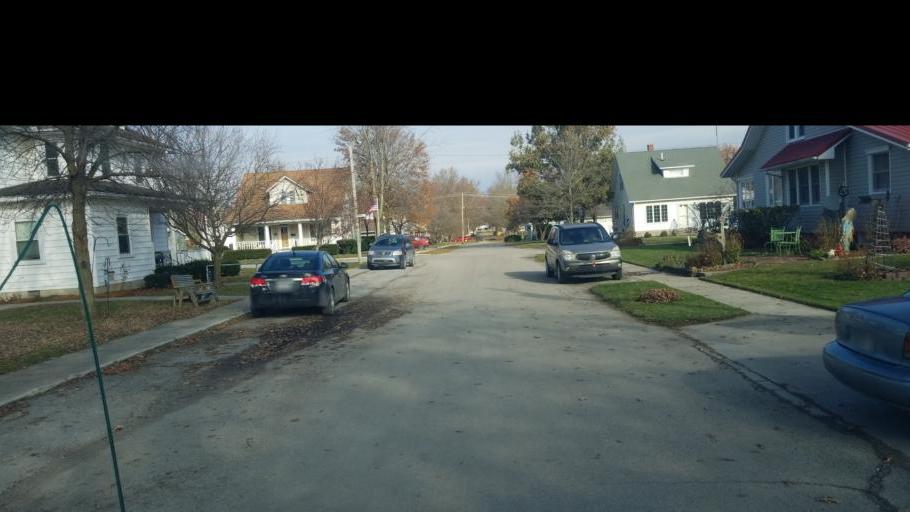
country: US
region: Indiana
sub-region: Adams County
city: Berne
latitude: 40.6609
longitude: -84.9527
